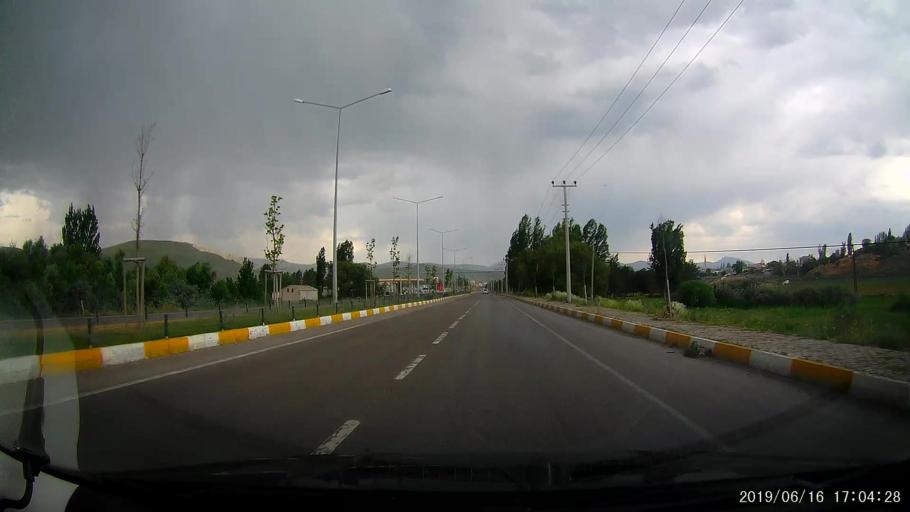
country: TR
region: Erzurum
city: Askale
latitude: 39.9258
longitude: 40.7088
